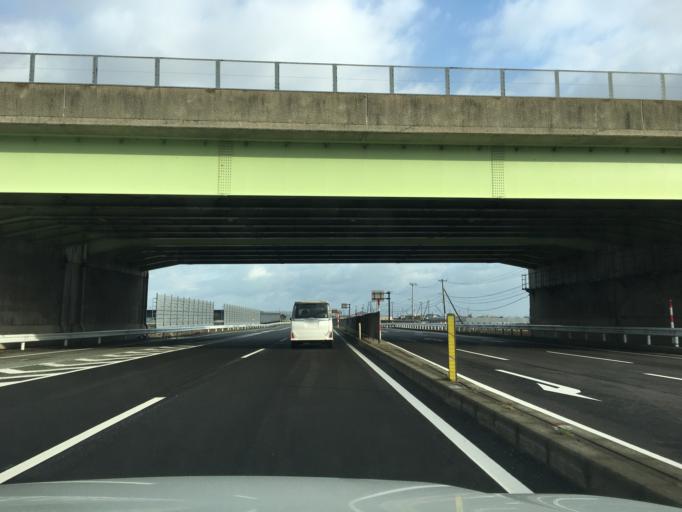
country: JP
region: Yamagata
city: Sakata
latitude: 38.8692
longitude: 139.8419
